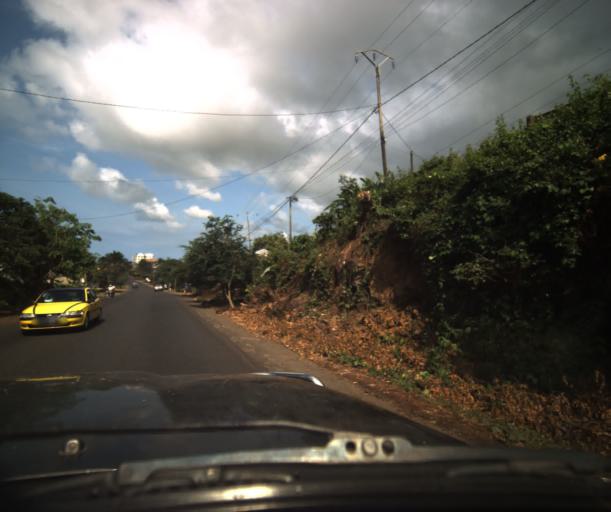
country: CM
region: South-West Province
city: Limbe
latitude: 4.0184
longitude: 9.1725
